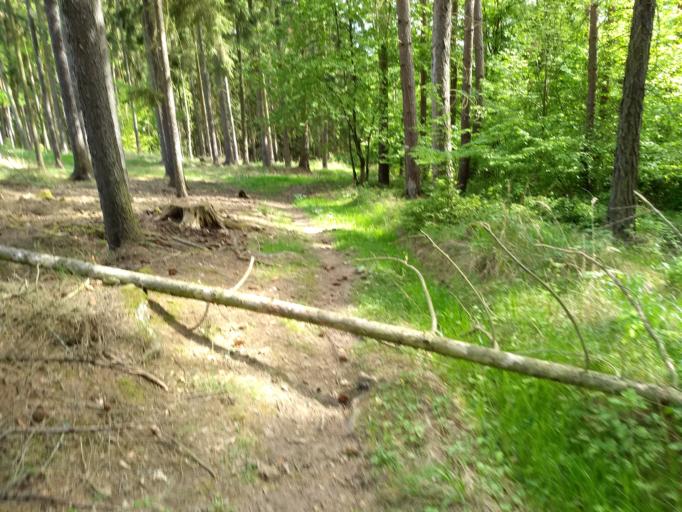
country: CZ
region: Central Bohemia
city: Unhost'
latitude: 50.0408
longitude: 14.1455
